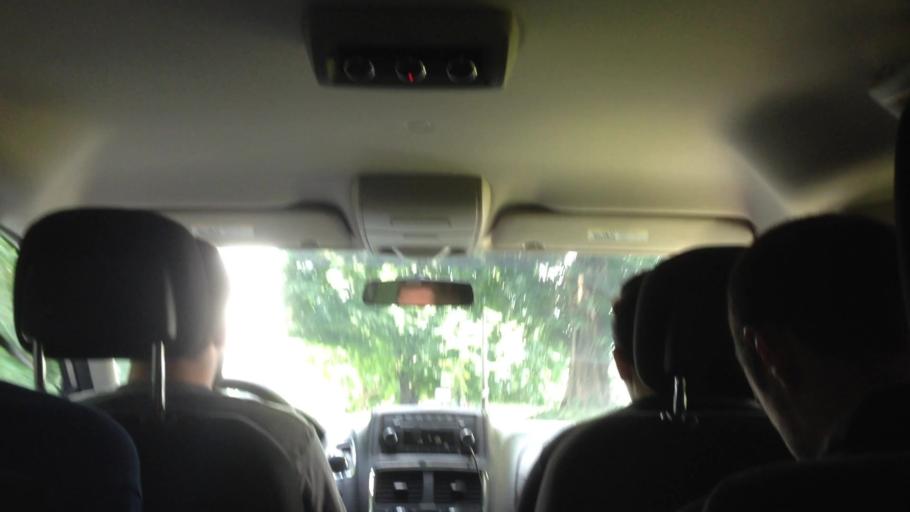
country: US
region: New York
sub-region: Dutchess County
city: Tivoli
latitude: 42.0535
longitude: -73.8802
